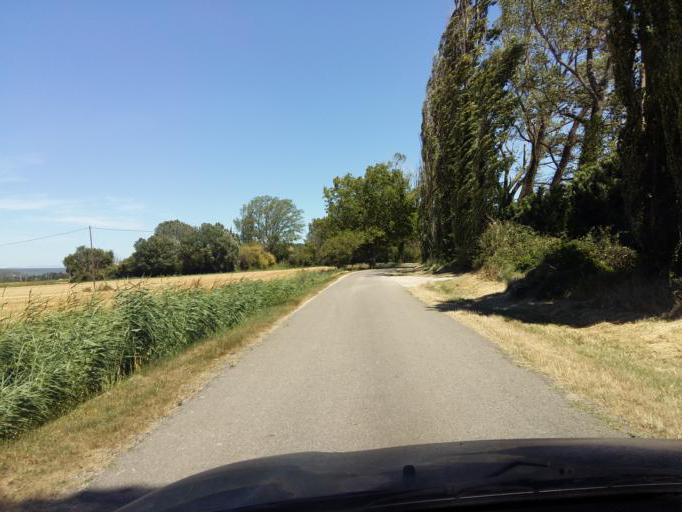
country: FR
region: Provence-Alpes-Cote d'Azur
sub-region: Departement du Vaucluse
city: Piolenc
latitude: 44.1659
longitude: 4.7402
